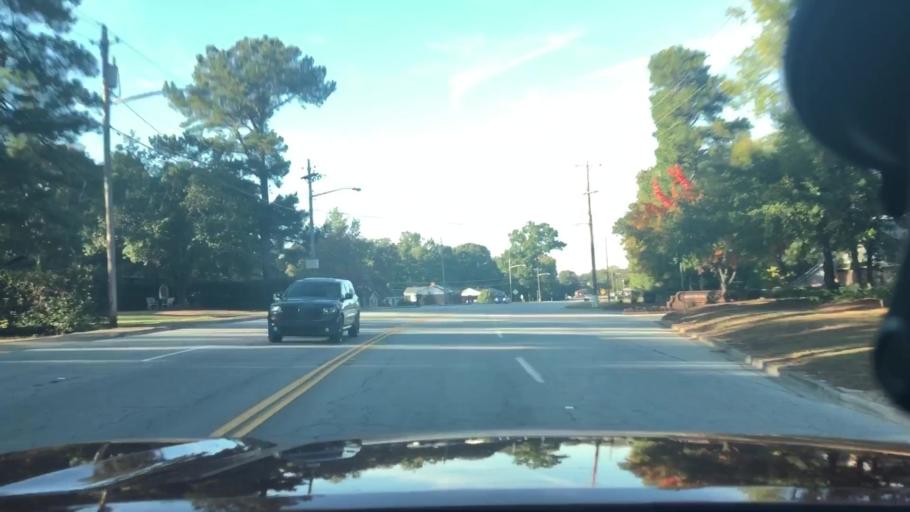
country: US
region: South Carolina
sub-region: Greenwood County
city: Greenwood
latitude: 34.2243
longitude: -82.1416
